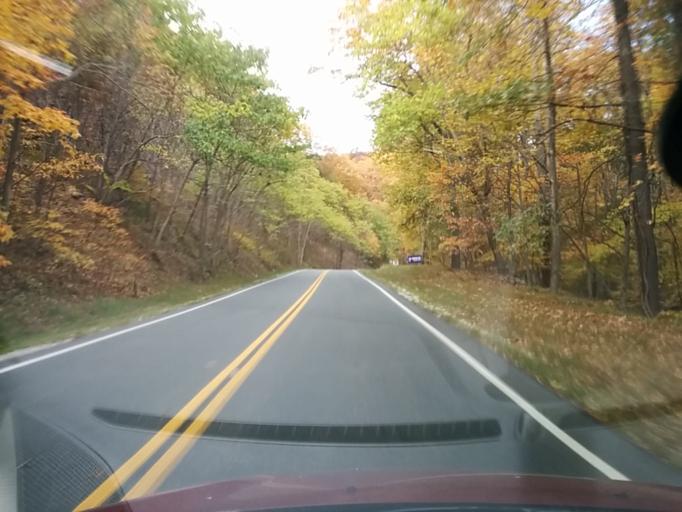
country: US
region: Virginia
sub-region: Nelson County
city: Nellysford
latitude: 37.8932
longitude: -78.9737
